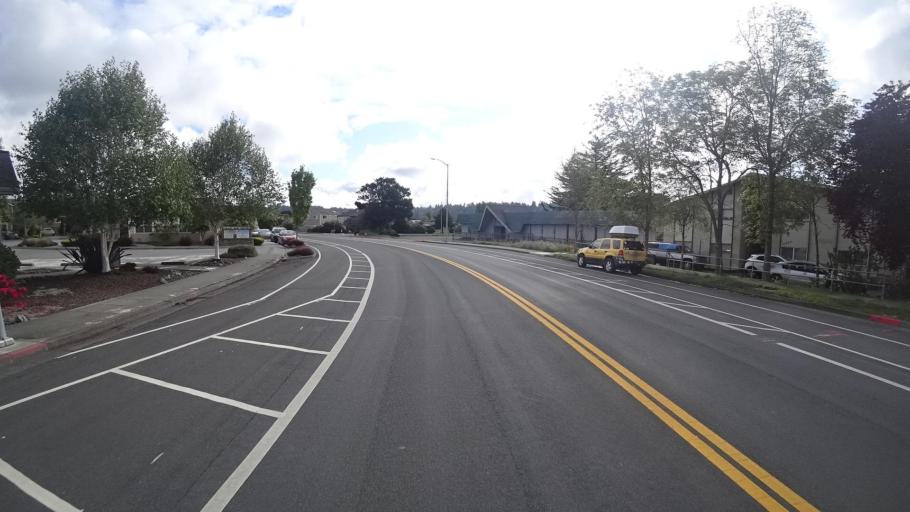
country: US
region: California
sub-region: Humboldt County
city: Arcata
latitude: 40.9004
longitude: -124.0821
